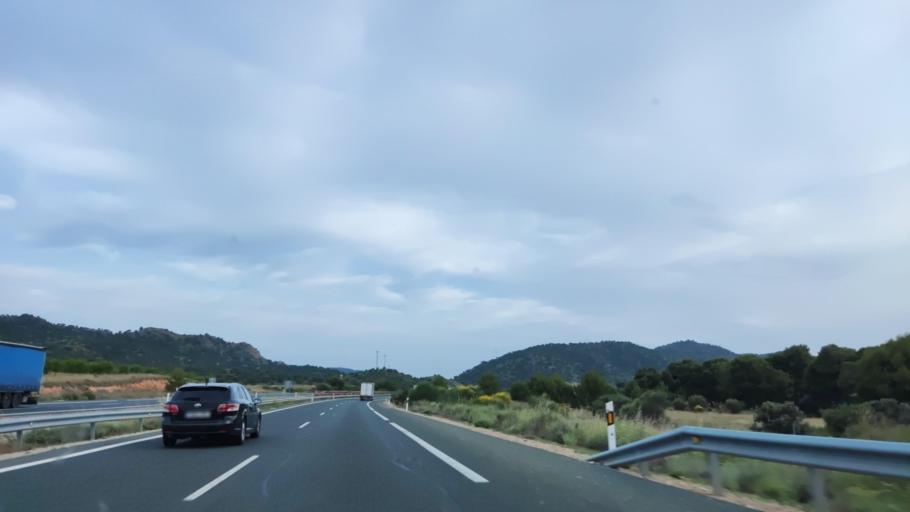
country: ES
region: Castille-La Mancha
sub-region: Provincia de Albacete
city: Tobarra
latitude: 38.6856
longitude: -1.6710
